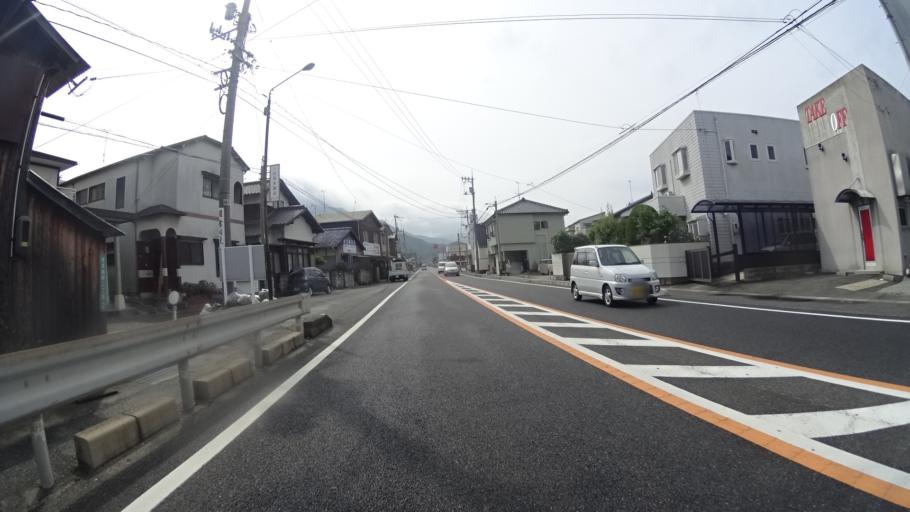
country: JP
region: Yamaguchi
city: Shimonoseki
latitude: 34.0724
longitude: 130.8982
